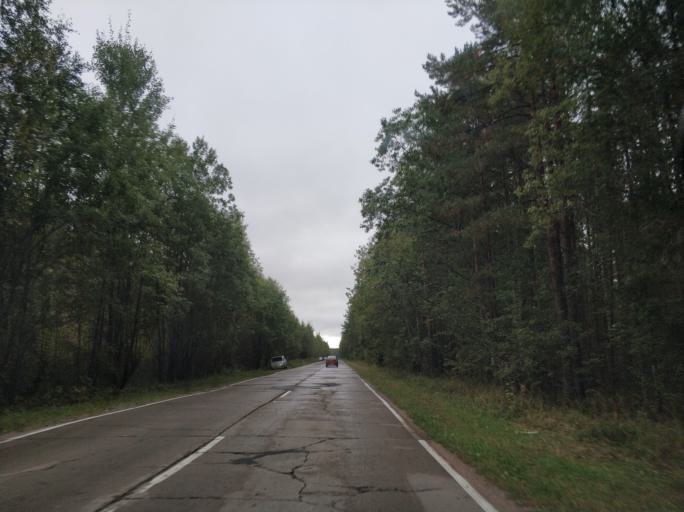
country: RU
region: Leningrad
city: Borisova Griva
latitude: 60.1734
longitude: 30.9194
